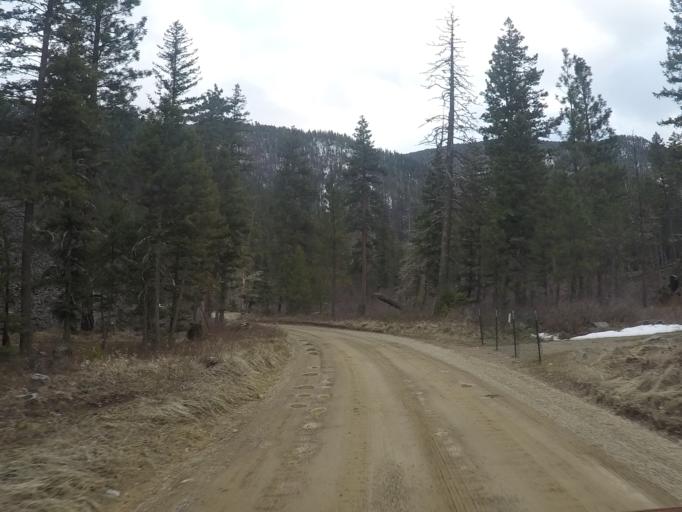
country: US
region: Montana
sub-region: Missoula County
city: Clinton
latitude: 46.5660
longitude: -113.7002
